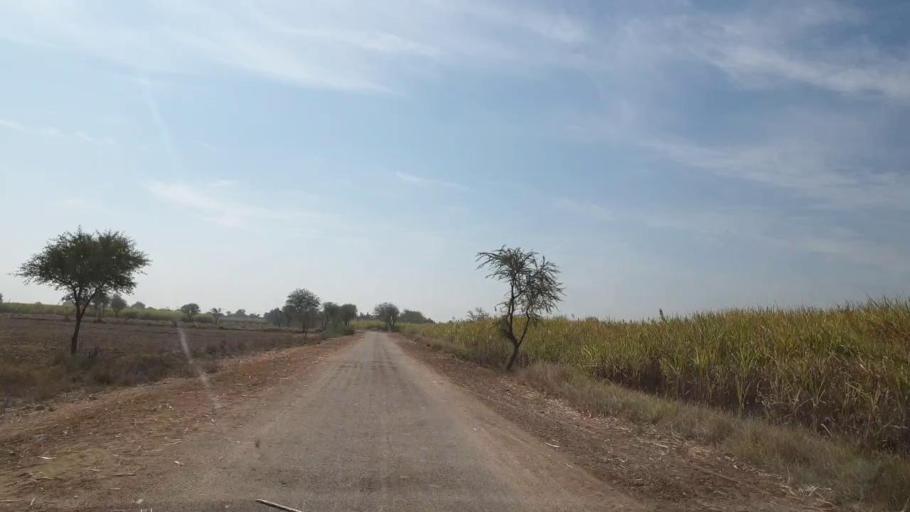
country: PK
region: Sindh
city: Mirpur Khas
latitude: 25.5282
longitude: 69.1452
